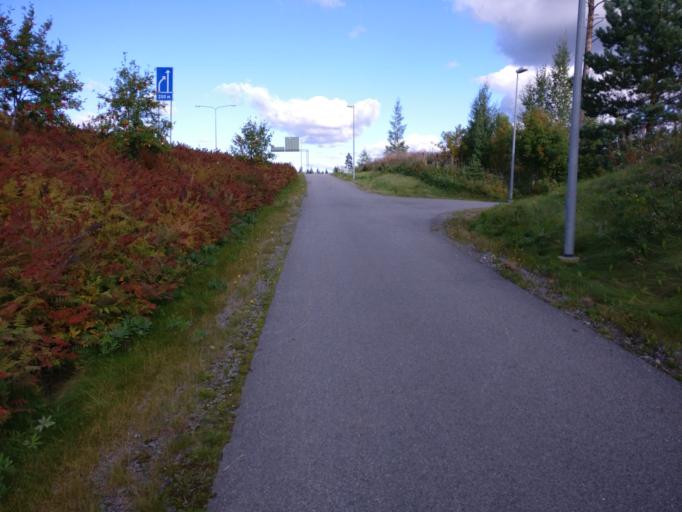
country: FI
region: Pirkanmaa
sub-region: Tampere
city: Lempaeaelae
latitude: 61.3662
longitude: 23.7991
